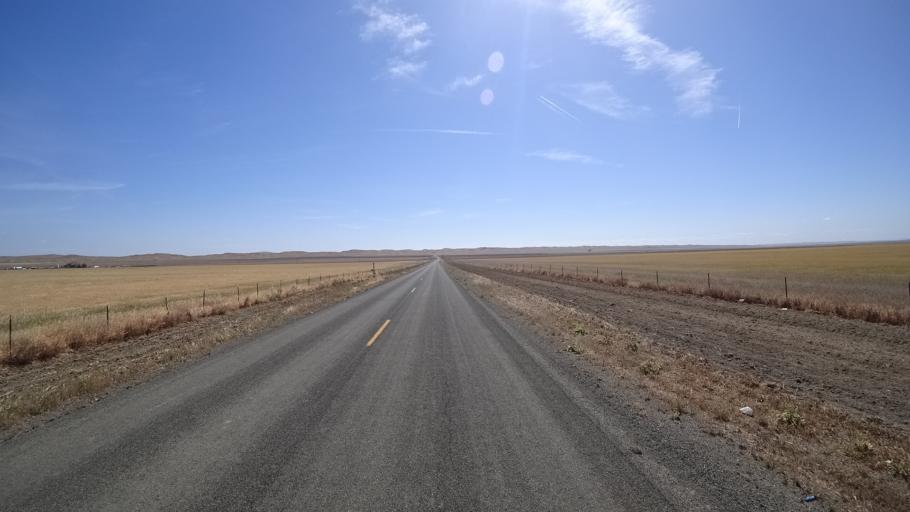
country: US
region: California
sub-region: Kings County
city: Avenal
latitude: 35.9352
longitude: -120.0644
